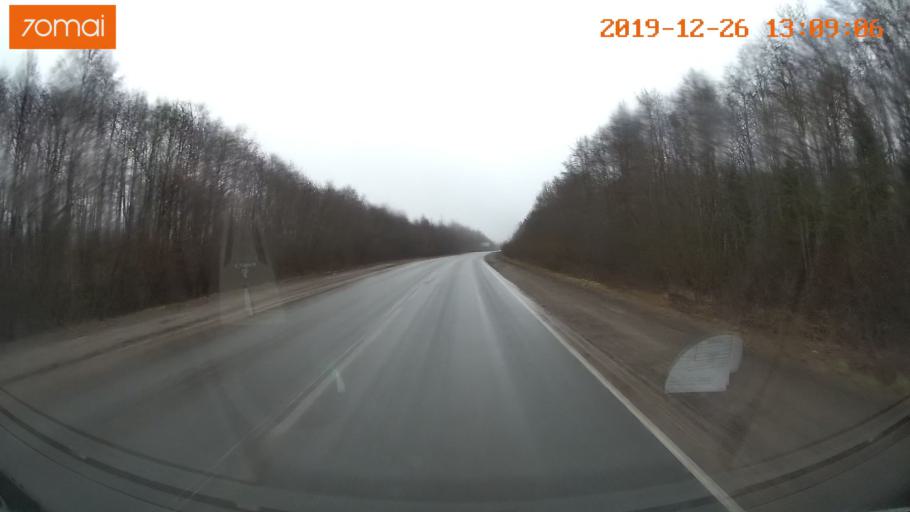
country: RU
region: Vologda
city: Cherepovets
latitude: 59.0508
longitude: 37.9502
